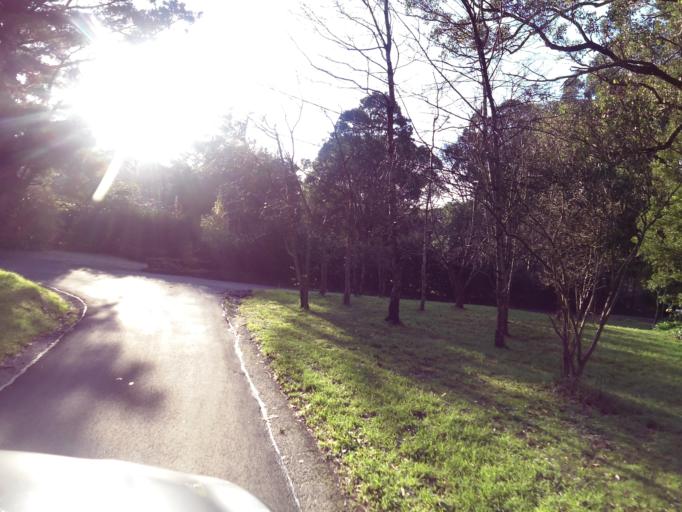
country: AU
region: Victoria
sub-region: Yarra Ranges
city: Ferny Creek
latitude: -37.8744
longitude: 145.3238
